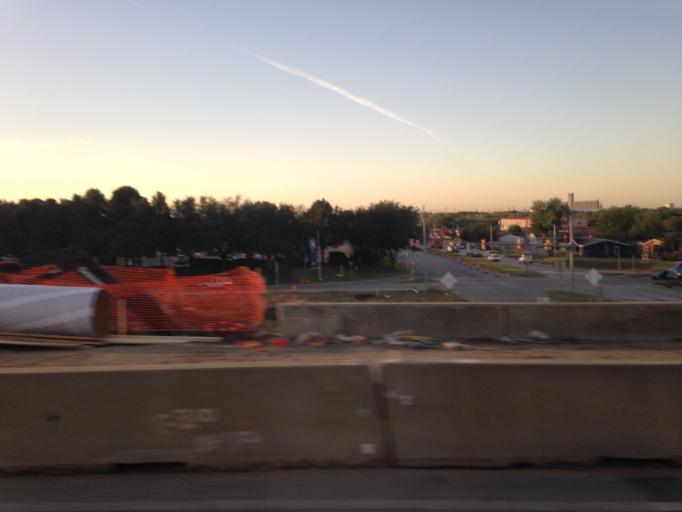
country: US
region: Texas
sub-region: Tarrant County
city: Blue Mound
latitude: 32.8396
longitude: -97.3211
